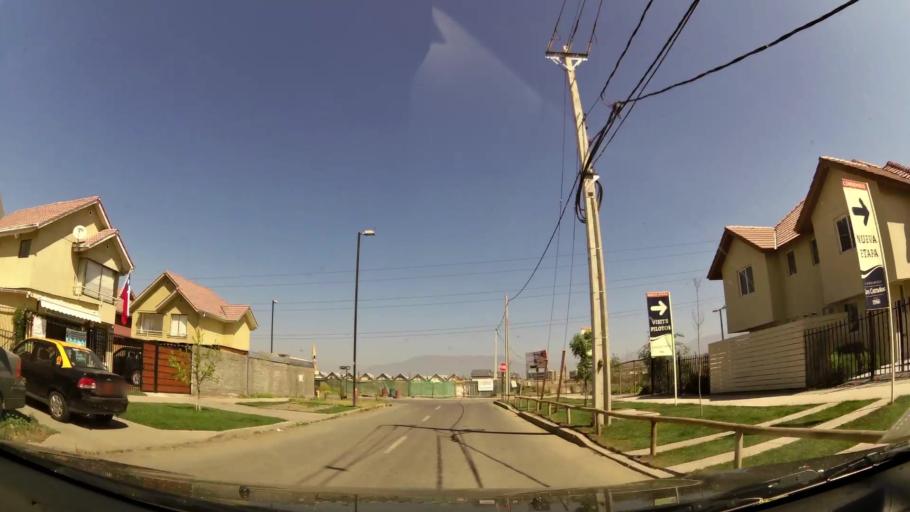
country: CL
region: Santiago Metropolitan
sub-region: Provincia de Chacabuco
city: Chicureo Abajo
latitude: -33.3238
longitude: -70.7552
